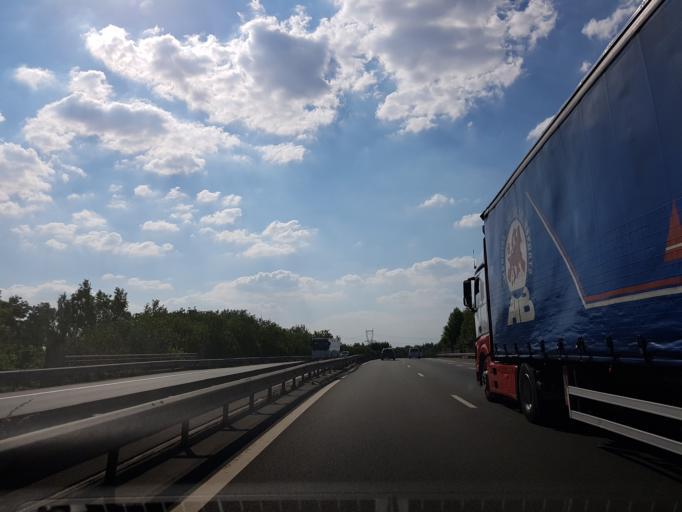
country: FR
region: Nord-Pas-de-Calais
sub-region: Departement du Nord
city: Somain
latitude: 50.3467
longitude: 3.2734
